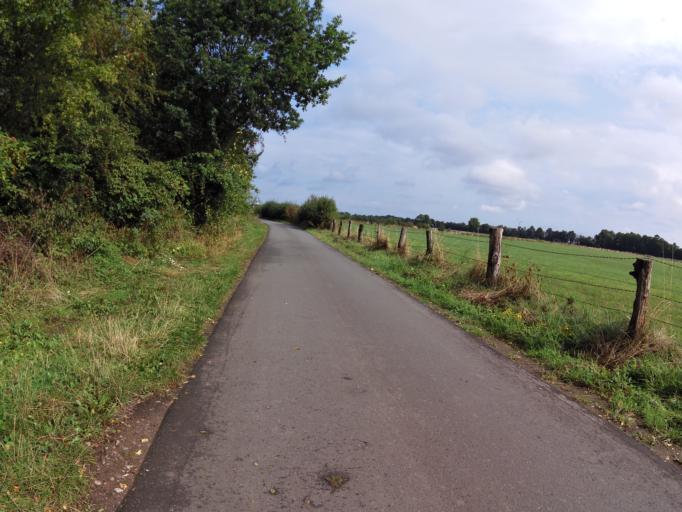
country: DE
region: Lower Saxony
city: Balge
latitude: 52.6938
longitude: 9.1793
